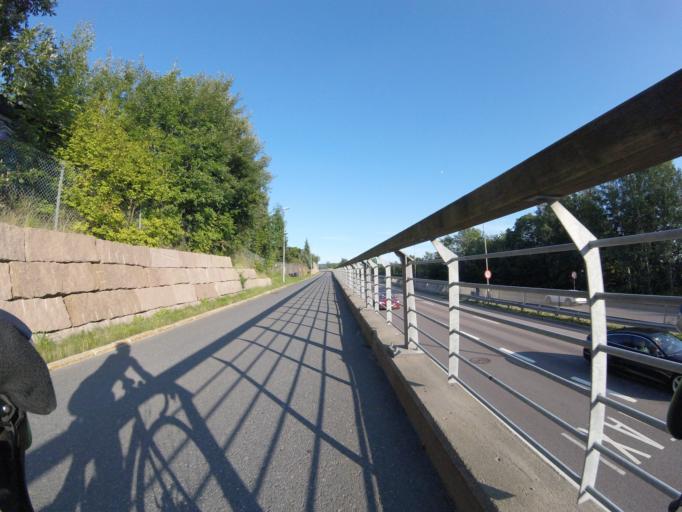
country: NO
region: Oslo
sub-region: Oslo
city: Oslo
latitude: 59.9440
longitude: 10.8241
